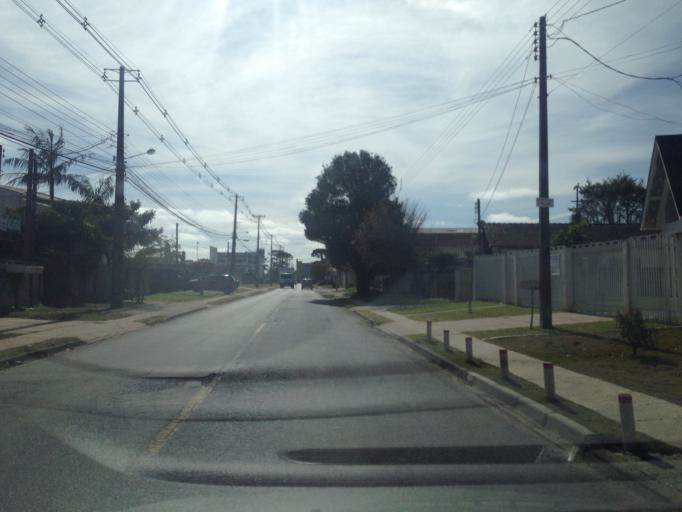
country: BR
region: Parana
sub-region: Sao Jose Dos Pinhais
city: Sao Jose dos Pinhais
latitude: -25.5599
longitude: -49.1710
